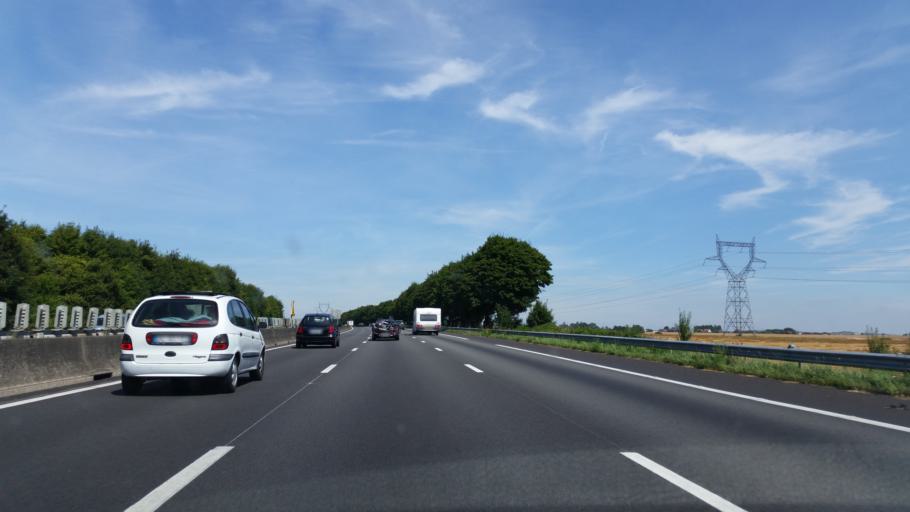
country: FR
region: Picardie
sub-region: Departement de la Somme
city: Peronne
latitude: 49.8989
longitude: 2.8466
